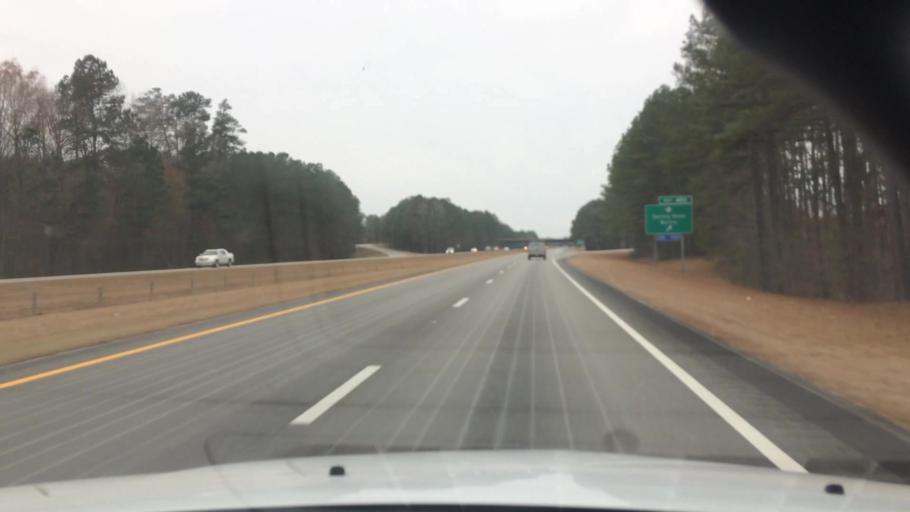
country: US
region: North Carolina
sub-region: Nash County
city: Spring Hope
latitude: 35.9311
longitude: -78.0908
